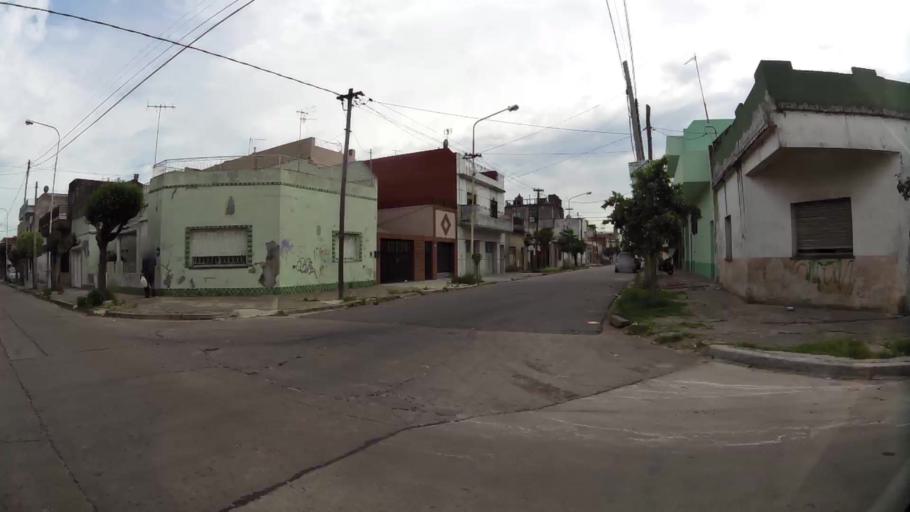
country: AR
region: Buenos Aires F.D.
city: Villa Lugano
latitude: -34.6830
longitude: -58.4978
